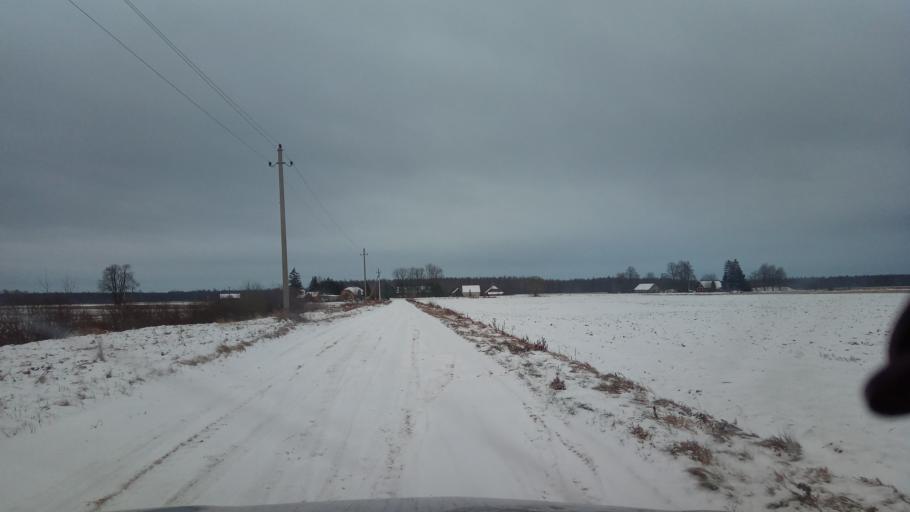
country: LT
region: Vilnius County
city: Ukmerge
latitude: 55.4784
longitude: 24.6259
